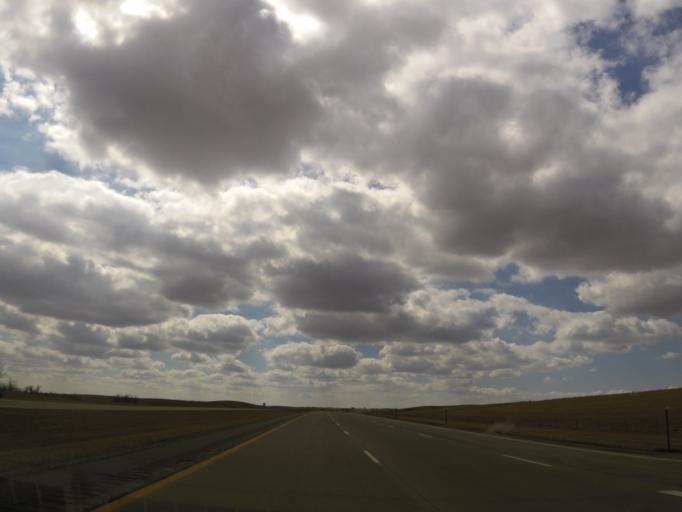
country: US
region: South Dakota
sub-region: Roberts County
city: Sisseton
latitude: 45.3999
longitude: -97.0237
